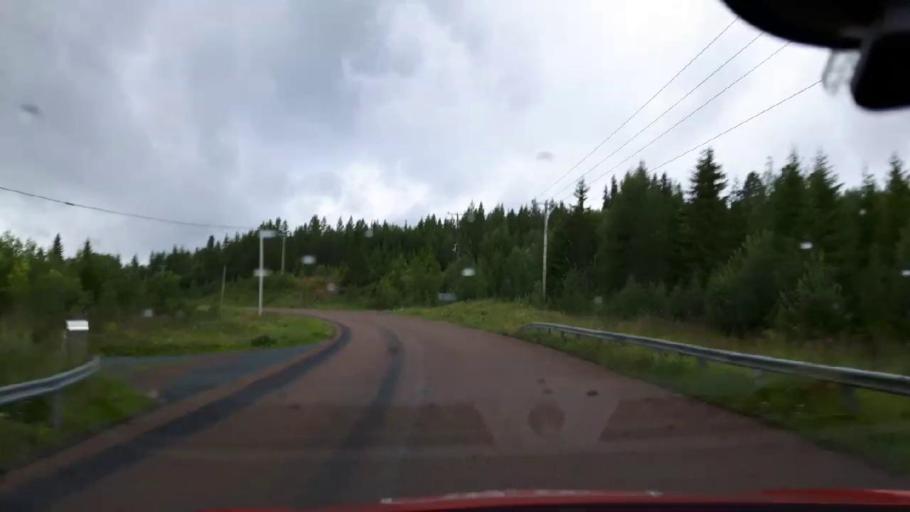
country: SE
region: Jaemtland
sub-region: Are Kommun
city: Jarpen
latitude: 63.3282
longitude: 13.6936
